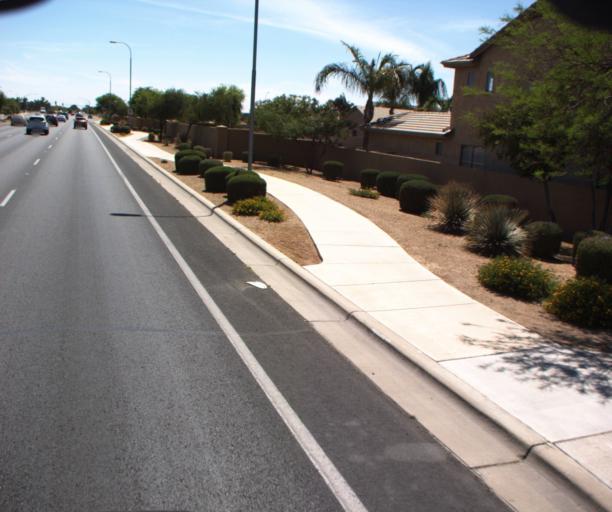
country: US
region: Arizona
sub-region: Maricopa County
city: Chandler
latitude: 33.2657
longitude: -111.8415
